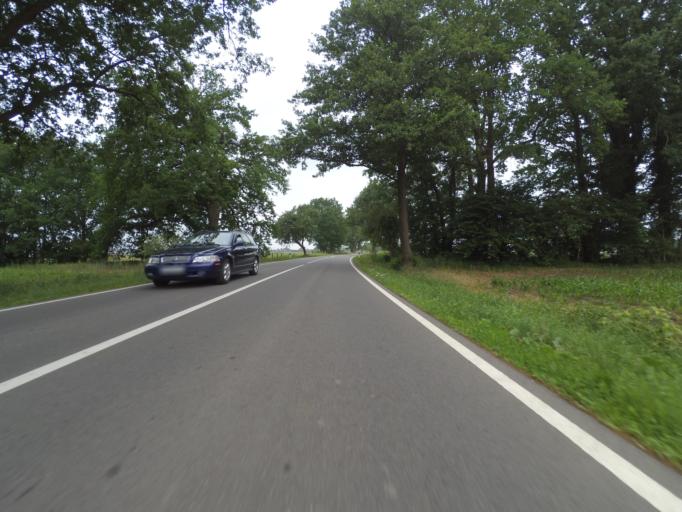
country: DE
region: Mecklenburg-Vorpommern
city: Domsuhl
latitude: 53.4847
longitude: 11.7480
